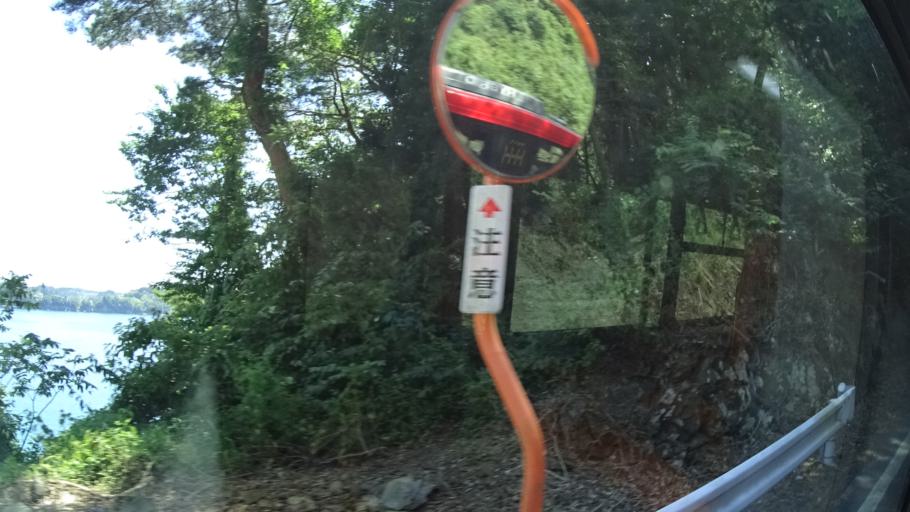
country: JP
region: Iwate
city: Ofunato
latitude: 38.9911
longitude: 141.7120
